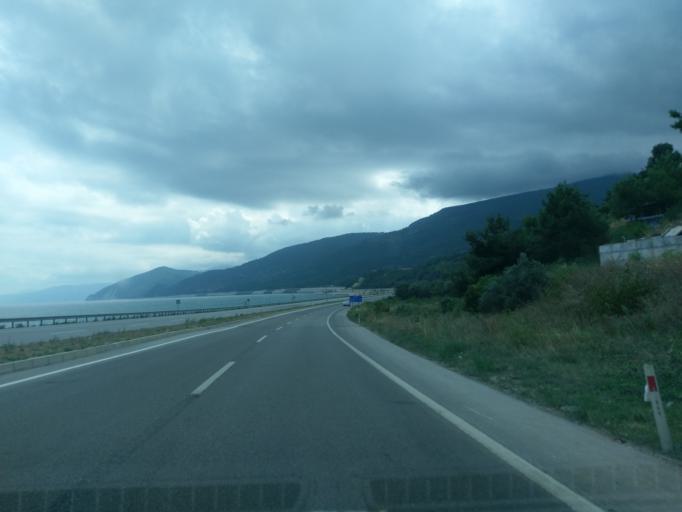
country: TR
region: Sinop
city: Gerze
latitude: 41.7815
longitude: 35.2014
